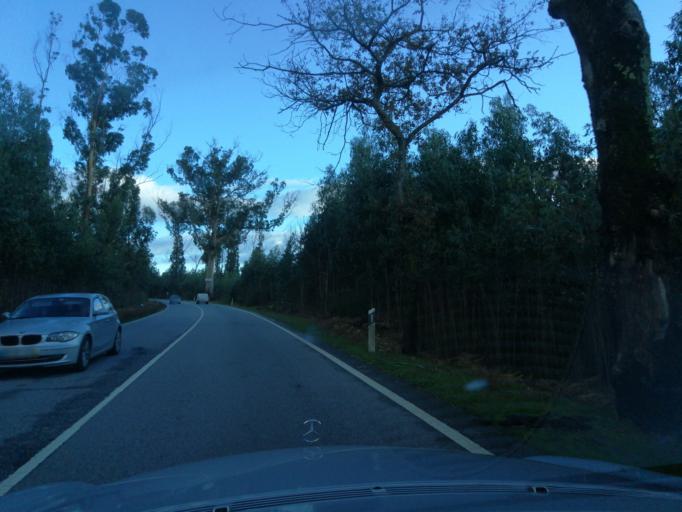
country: PT
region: Braga
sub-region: Esposende
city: Marinhas
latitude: 41.5745
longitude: -8.7212
